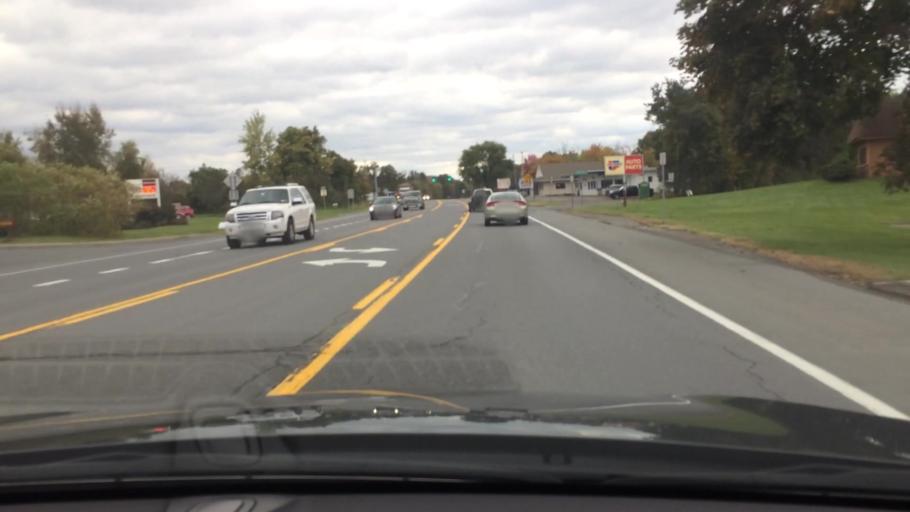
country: US
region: New York
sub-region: Columbia County
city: Valatie
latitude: 42.4268
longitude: -73.6891
